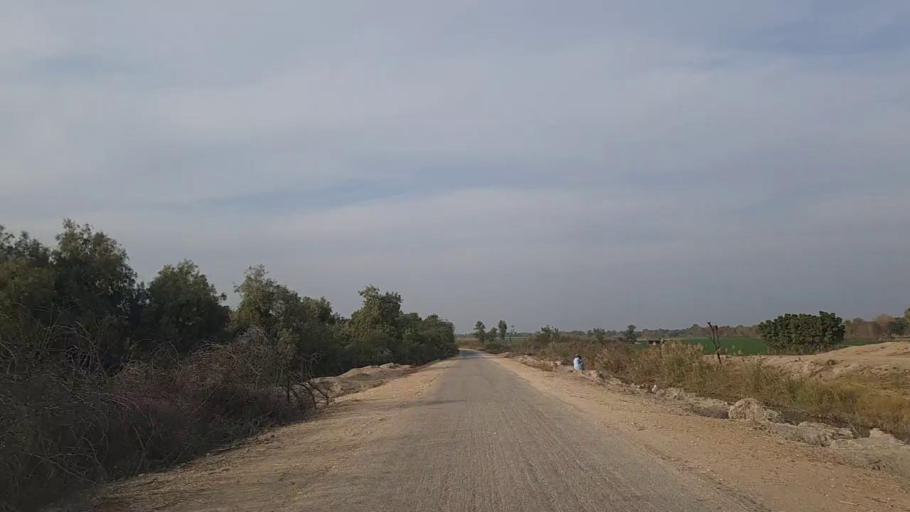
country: PK
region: Sindh
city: Daur
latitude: 26.4837
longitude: 68.4640
